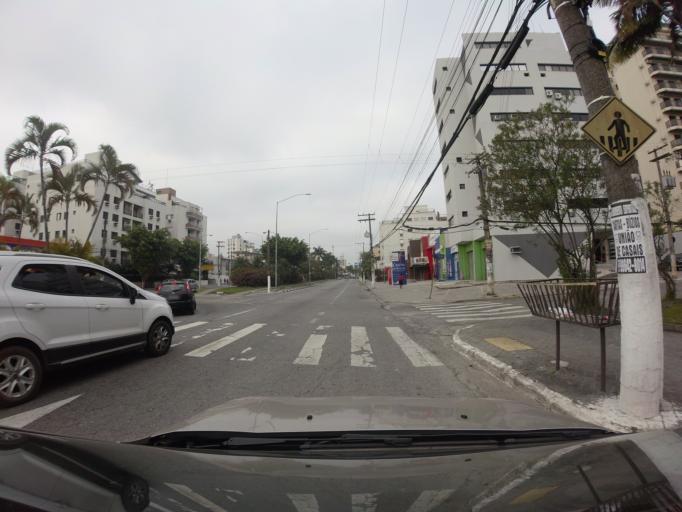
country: BR
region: Sao Paulo
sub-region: Guaruja
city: Guaruja
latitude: -23.9845
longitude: -46.2393
